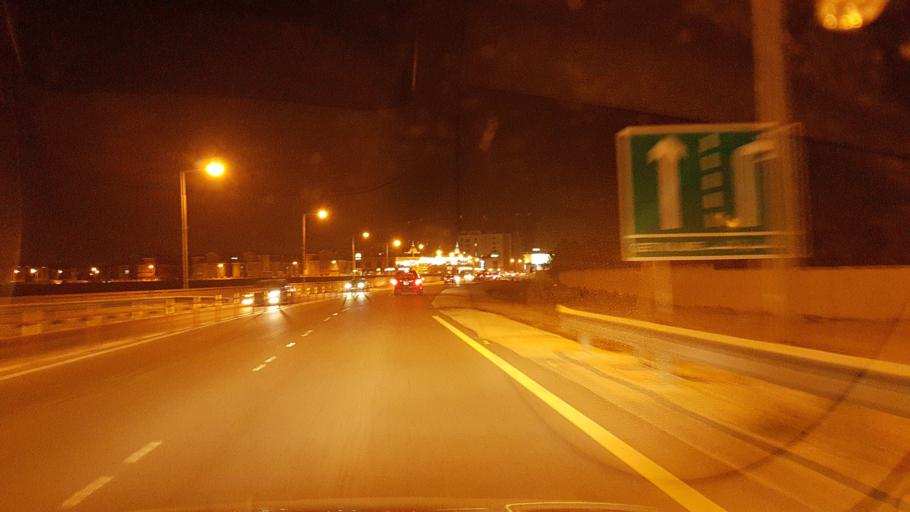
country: BH
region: Central Governorate
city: Madinat Hamad
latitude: 26.1757
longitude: 50.4811
